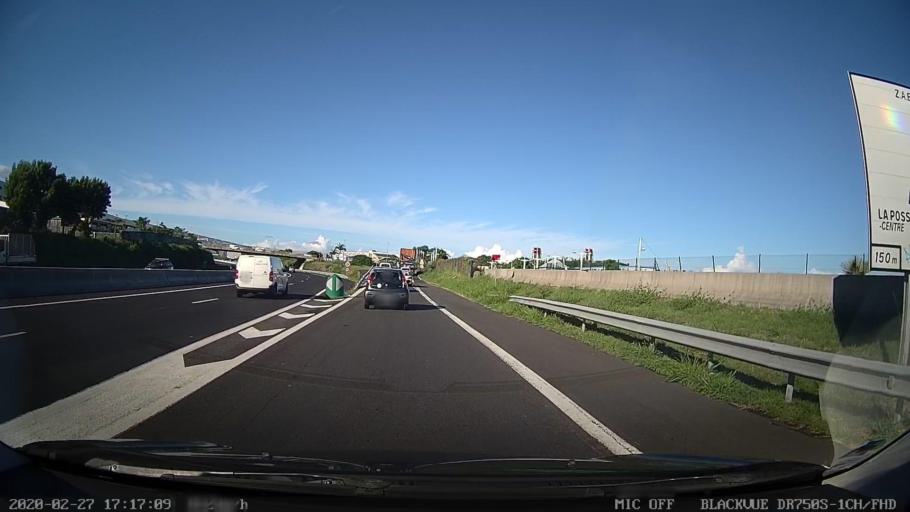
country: RE
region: Reunion
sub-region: Reunion
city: La Possession
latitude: -20.9276
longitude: 55.3321
